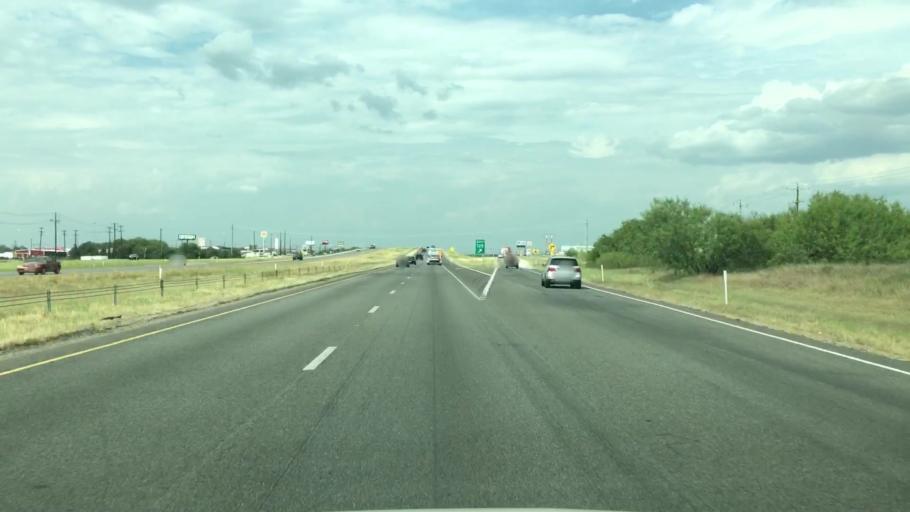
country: US
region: Texas
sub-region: Bexar County
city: Elmendorf
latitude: 29.2122
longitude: -98.4147
